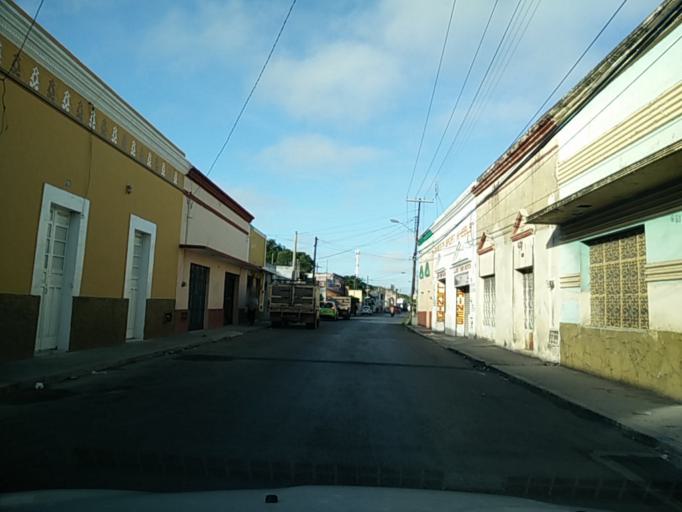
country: MX
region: Yucatan
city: Merida
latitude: 20.9668
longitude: -89.6384
